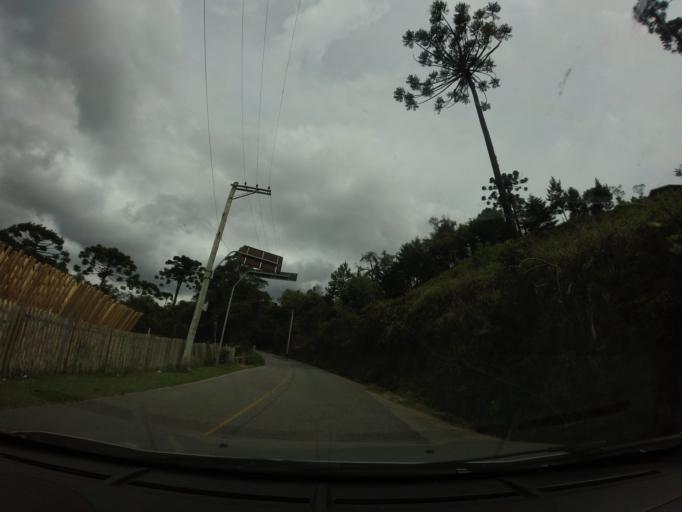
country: BR
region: Sao Paulo
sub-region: Campos Do Jordao
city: Campos do Jordao
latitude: -22.6745
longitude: -45.5905
